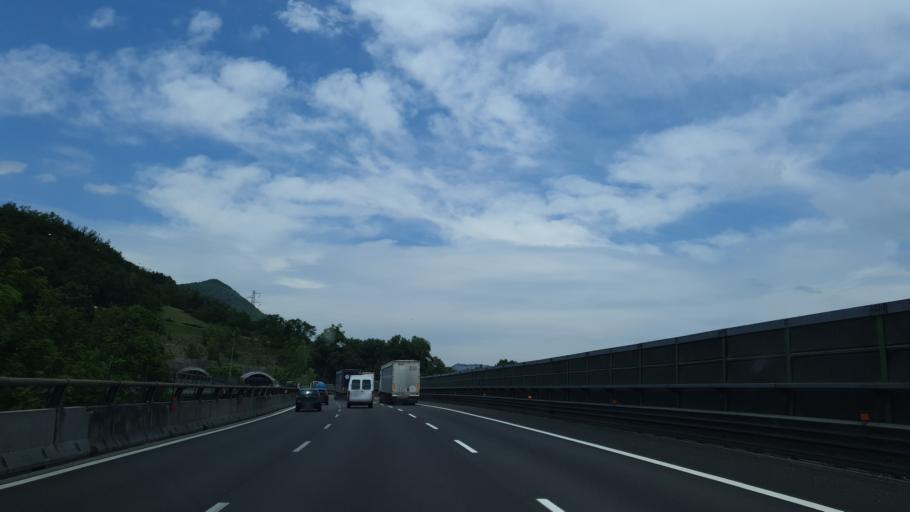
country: IT
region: Emilia-Romagna
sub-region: Provincia di Bologna
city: Vado
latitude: 44.3007
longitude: 11.2386
